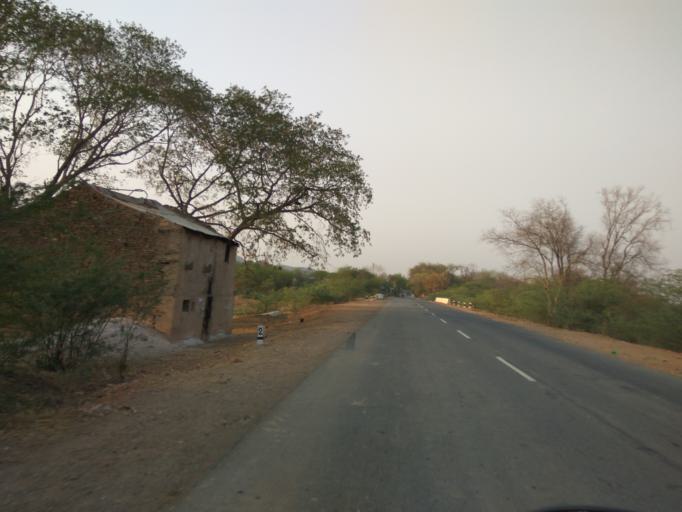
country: IN
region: Andhra Pradesh
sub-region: Prakasam
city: Cumbum
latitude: 15.6372
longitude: 79.1405
